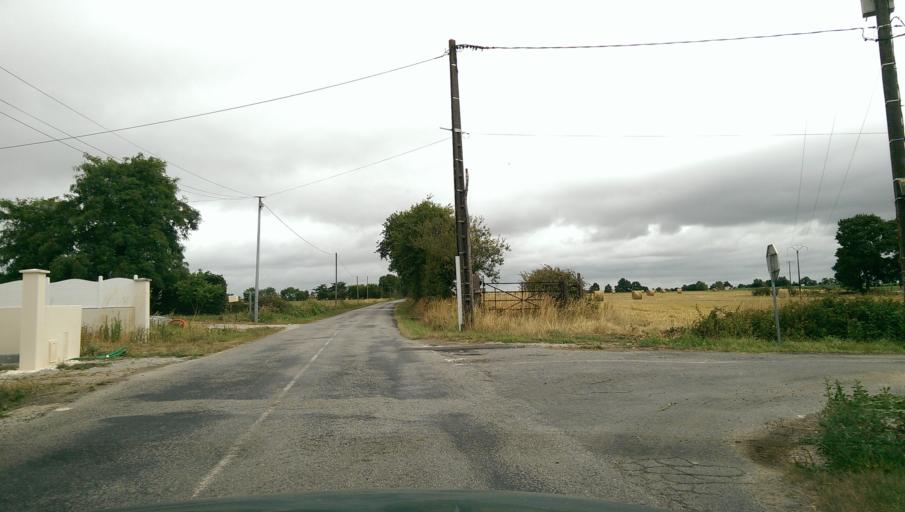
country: FR
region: Pays de la Loire
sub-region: Departement de la Loire-Atlantique
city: La Planche
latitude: 47.0324
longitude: -1.4023
